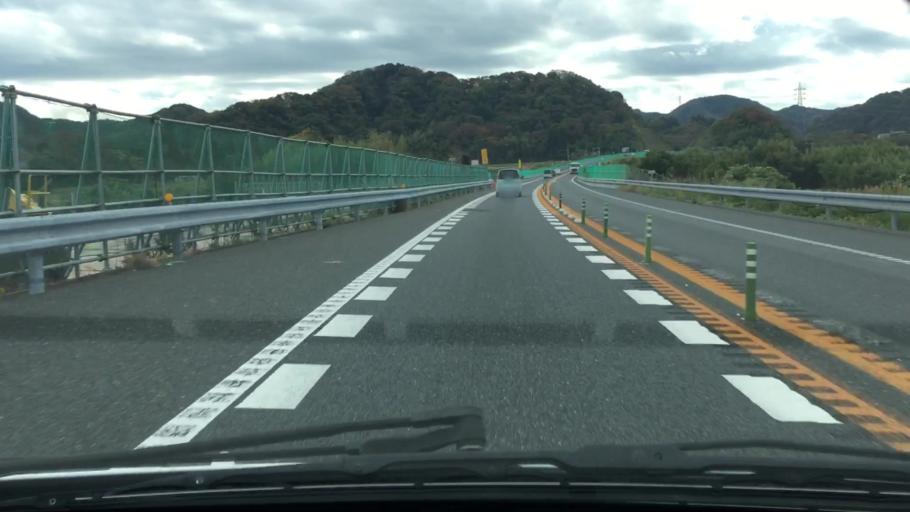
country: JP
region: Chiba
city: Kimitsu
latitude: 35.2167
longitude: 139.8859
